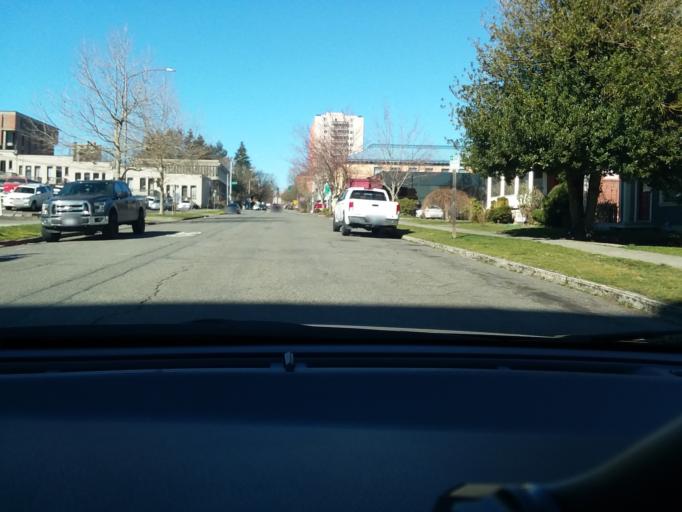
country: US
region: Washington
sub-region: Pierce County
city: Tacoma
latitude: 47.2517
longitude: -122.4427
